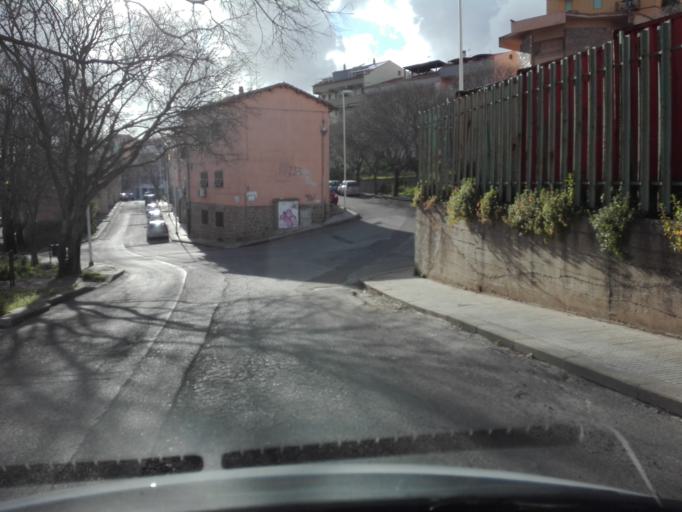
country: IT
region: Sardinia
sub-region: Provincia di Sassari
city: Sassari
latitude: 40.7334
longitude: 8.5673
